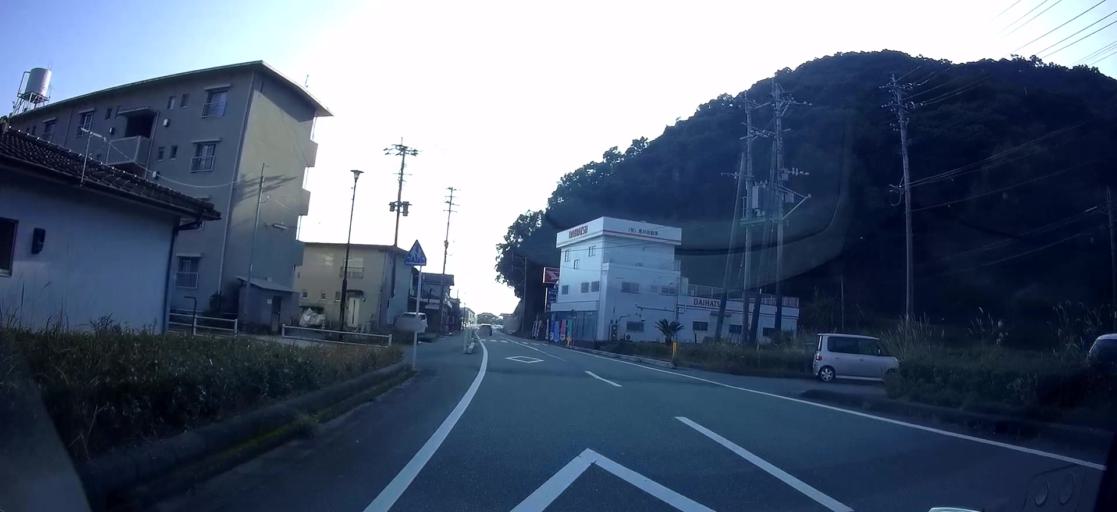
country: JP
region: Kumamoto
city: Minamata
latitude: 32.4084
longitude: 130.4041
